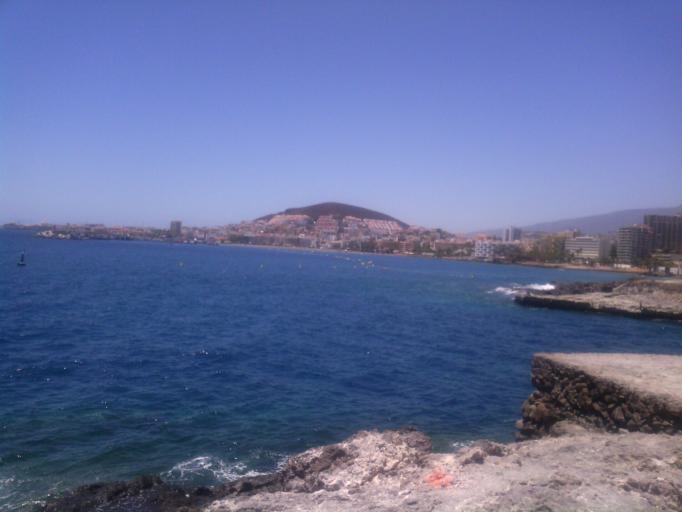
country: ES
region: Canary Islands
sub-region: Provincia de Santa Cruz de Tenerife
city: Playa de las Americas
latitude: 28.0429
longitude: -16.7111
